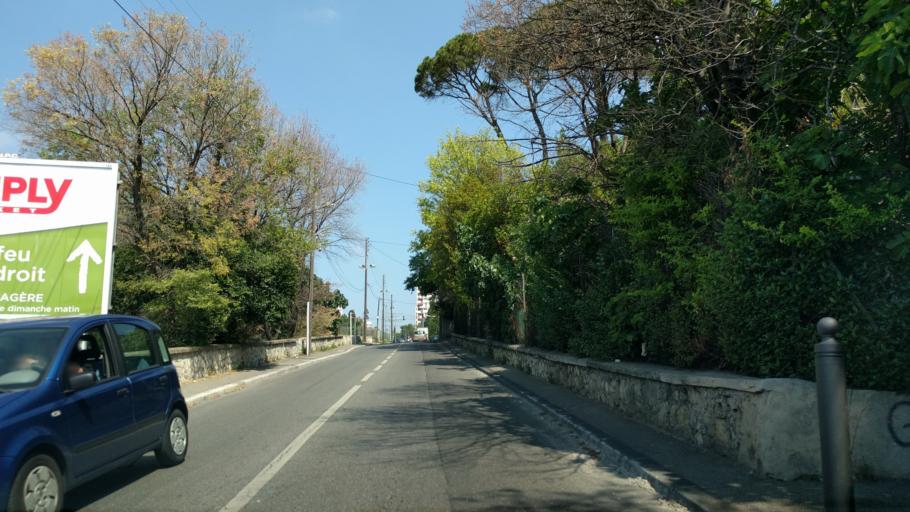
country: FR
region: Provence-Alpes-Cote d'Azur
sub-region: Departement des Bouches-du-Rhone
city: Marseille 11
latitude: 43.2908
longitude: 5.4362
